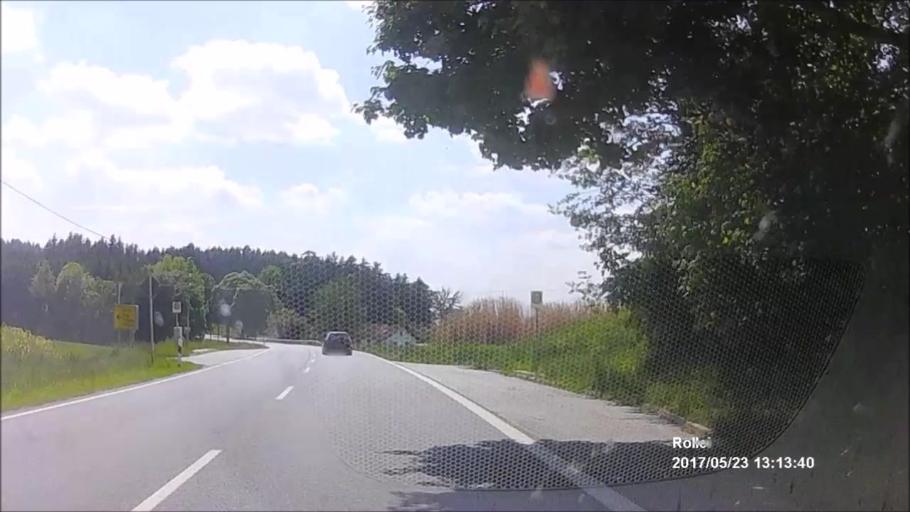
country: DE
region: Bavaria
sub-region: Lower Bavaria
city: Vilsheim
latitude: 48.4235
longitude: 12.1320
